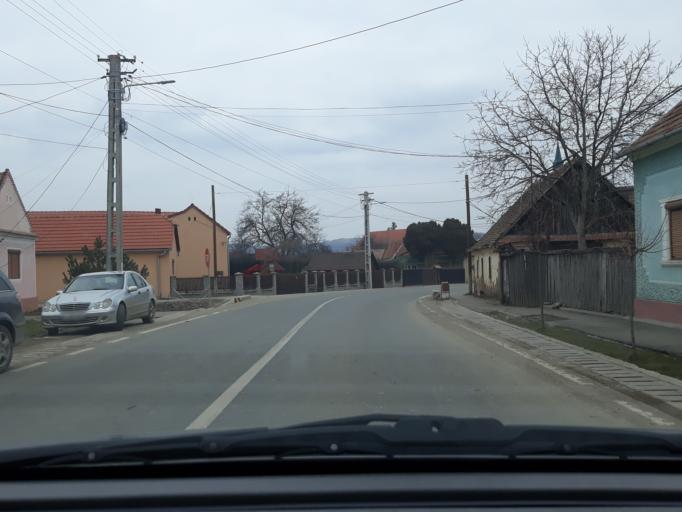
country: RO
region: Salaj
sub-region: Comuna Nusfalau
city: Nusfalau
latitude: 47.1948
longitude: 22.7011
